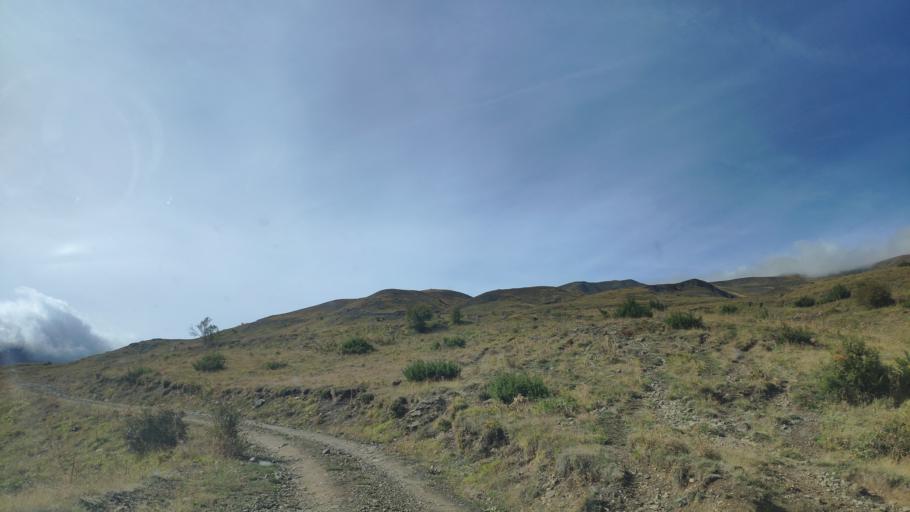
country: AL
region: Korce
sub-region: Rrethi i Kolonjes
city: Erseke
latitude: 40.3804
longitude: 20.8282
